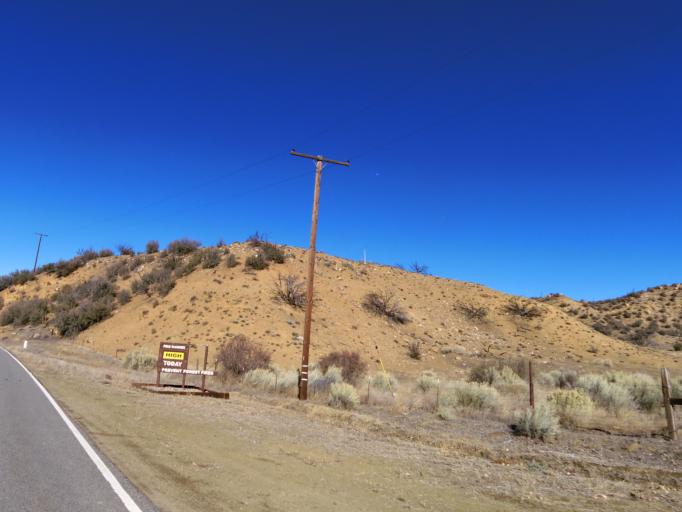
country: US
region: California
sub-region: Ventura County
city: Meiners Oaks
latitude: 34.6842
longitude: -119.3550
